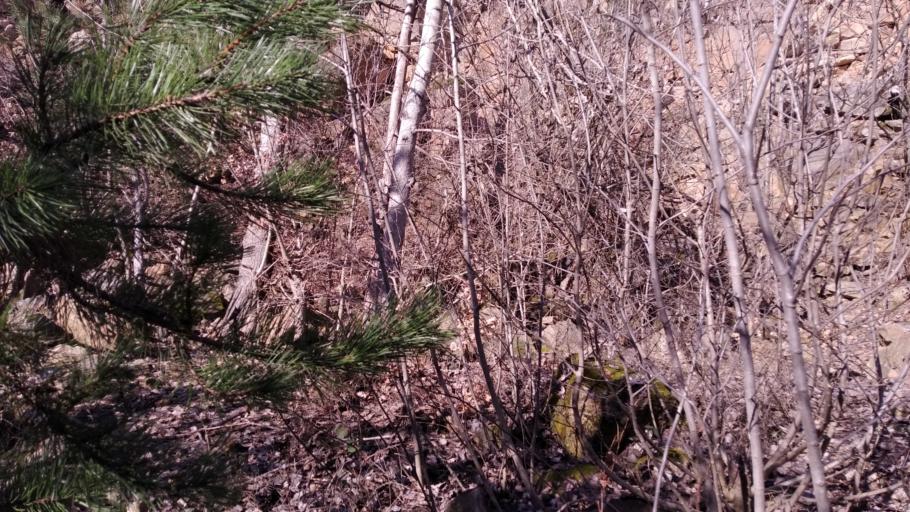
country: HU
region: Pest
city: Pilisborosjeno
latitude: 47.6118
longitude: 19.0045
